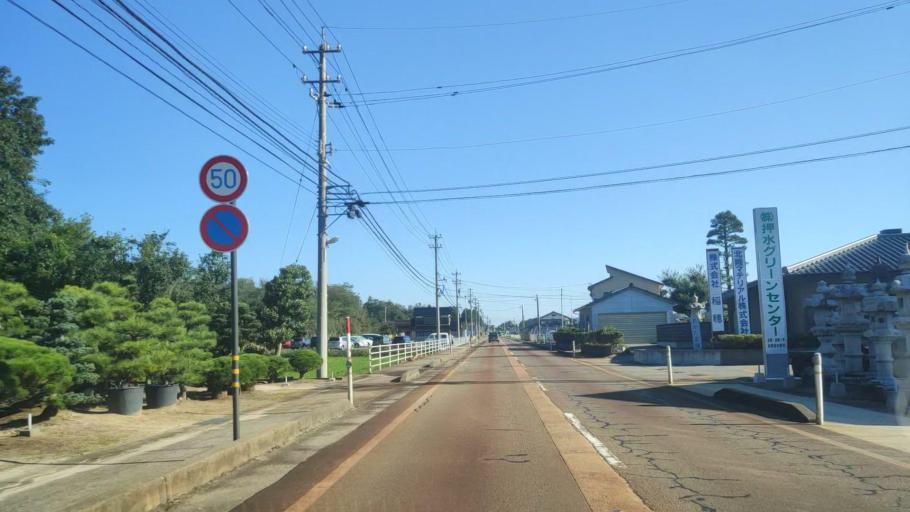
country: JP
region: Ishikawa
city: Hakui
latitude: 36.8110
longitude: 136.7549
